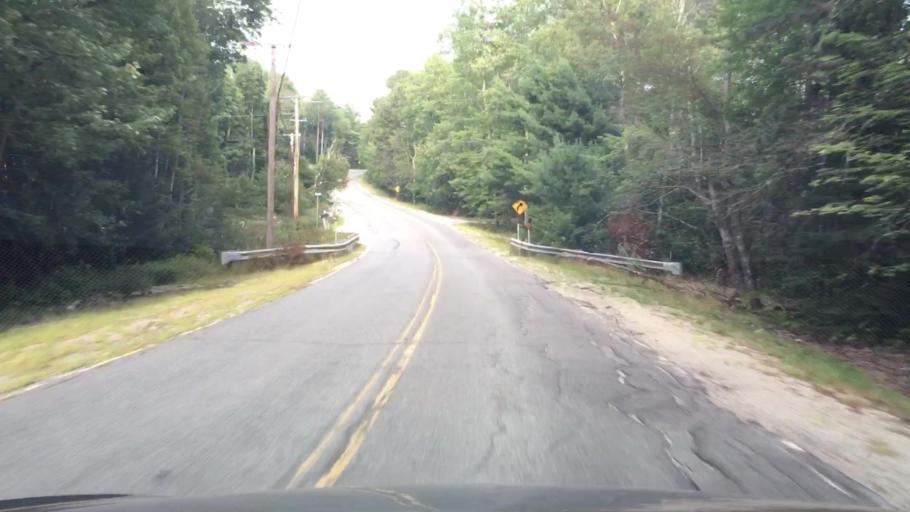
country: US
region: Maine
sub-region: Hancock County
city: Surry
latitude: 44.4978
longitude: -68.5408
